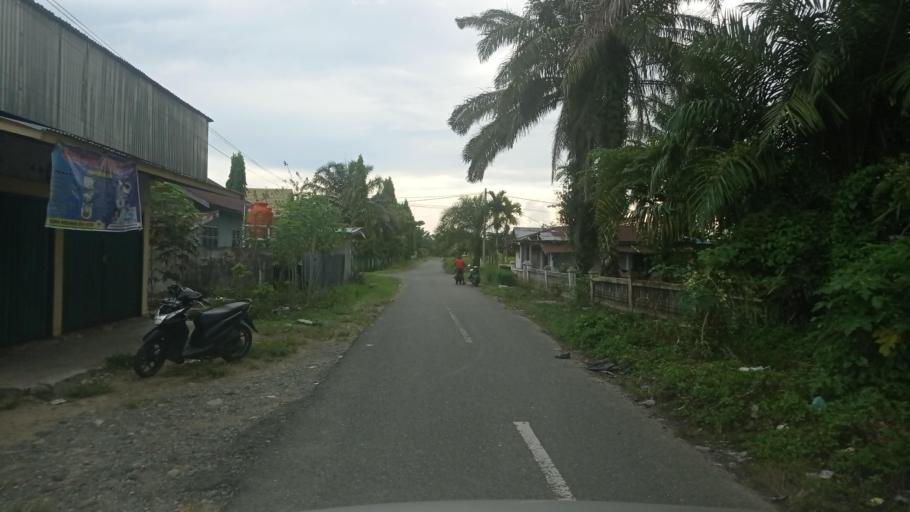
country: ID
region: Jambi
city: Sungai Penuh
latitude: -2.5585
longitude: 101.1041
